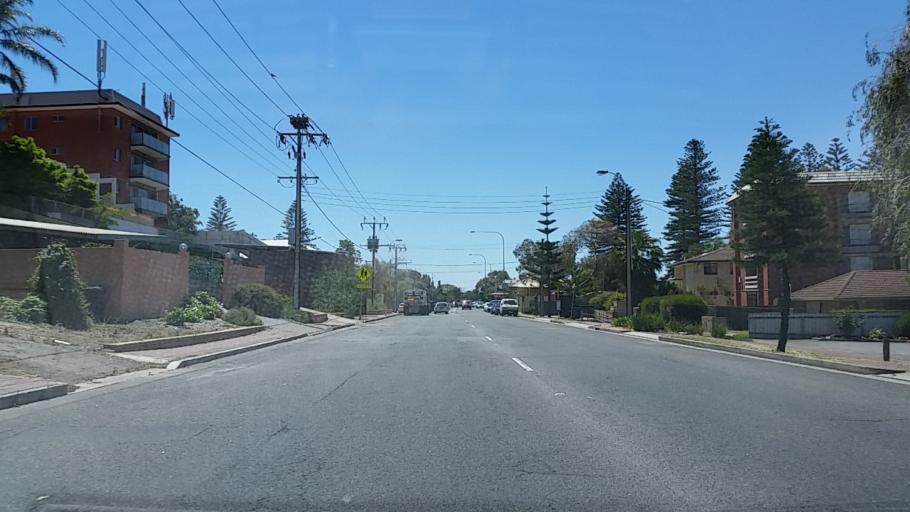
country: AU
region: South Australia
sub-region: Charles Sturt
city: Grange
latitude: -34.9038
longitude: 138.4911
